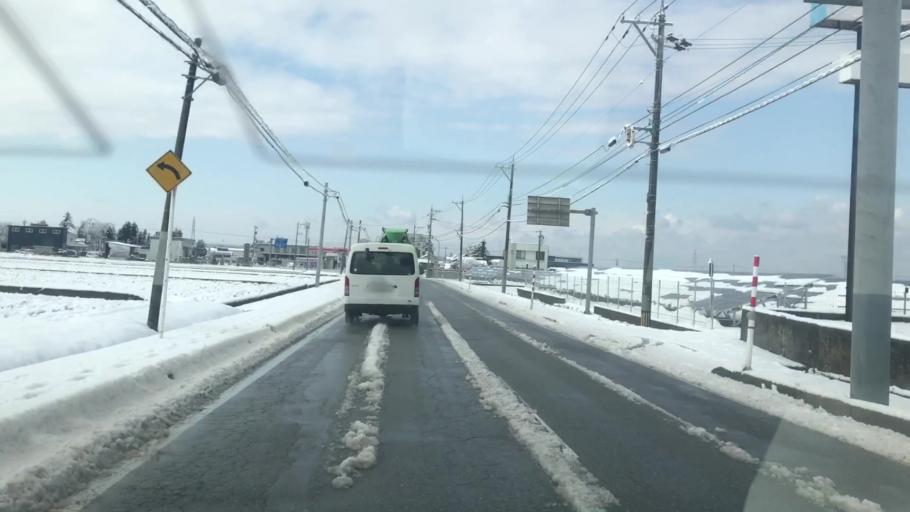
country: JP
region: Toyama
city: Toyama-shi
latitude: 36.6300
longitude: 137.2347
